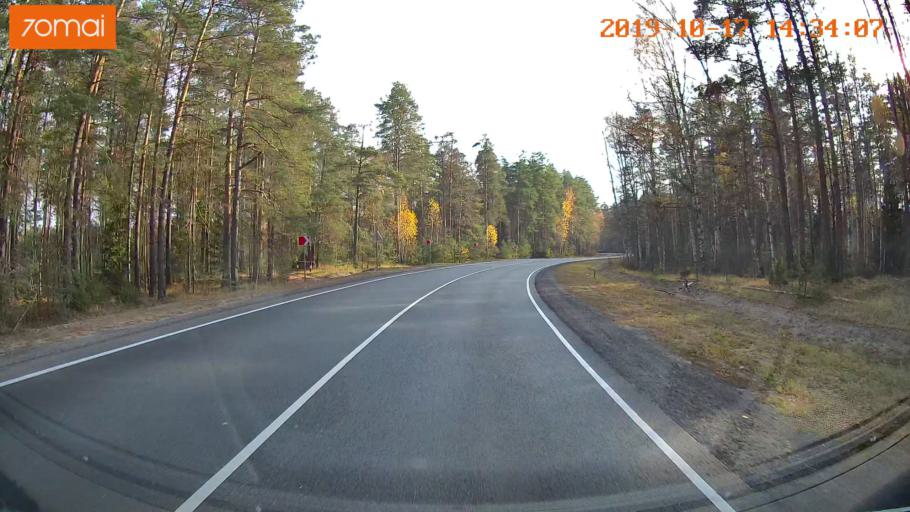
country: RU
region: Rjazan
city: Solotcha
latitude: 54.9164
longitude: 39.9978
